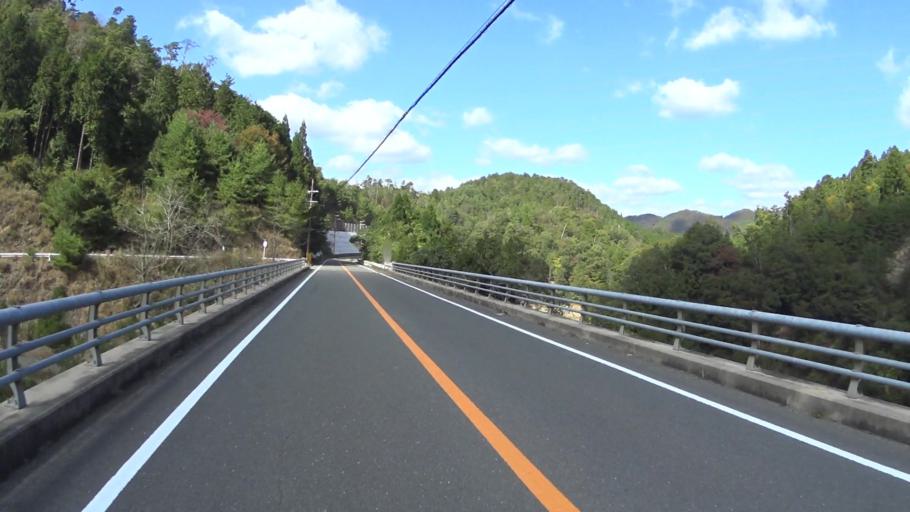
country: JP
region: Kyoto
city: Kameoka
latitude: 35.1334
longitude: 135.5371
